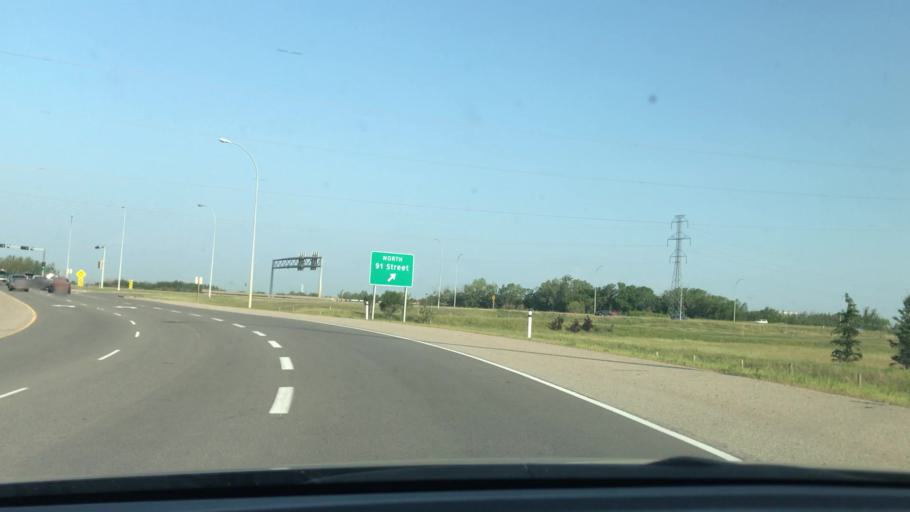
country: CA
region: Alberta
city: Beaumont
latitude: 53.4397
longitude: -113.4642
